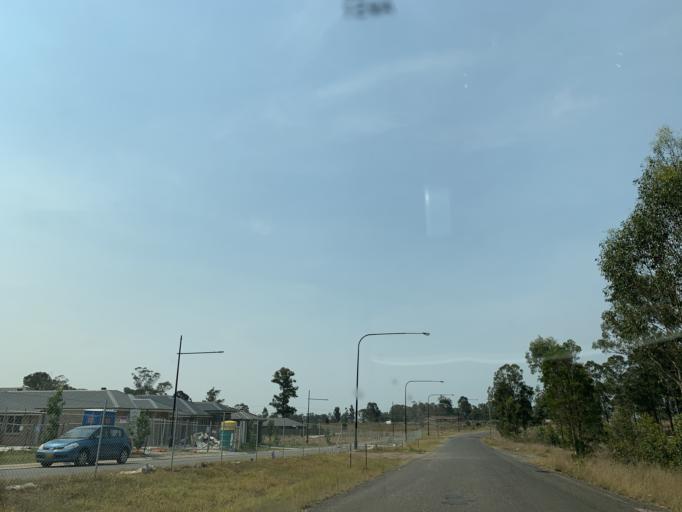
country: AU
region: New South Wales
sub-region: Blacktown
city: Blackett
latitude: -33.7134
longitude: 150.8208
